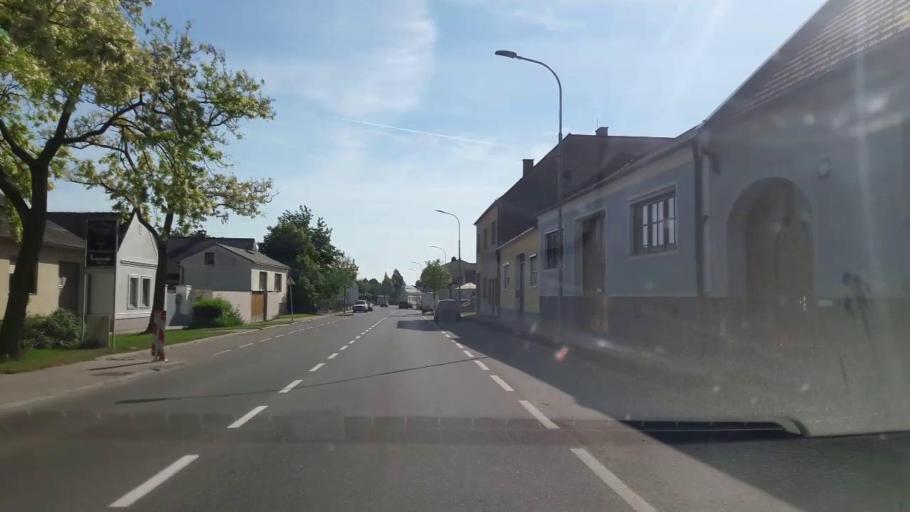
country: AT
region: Burgenland
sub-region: Eisenstadt-Umgebung
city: Trausdorf an der Wulka
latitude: 47.8132
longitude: 16.5533
